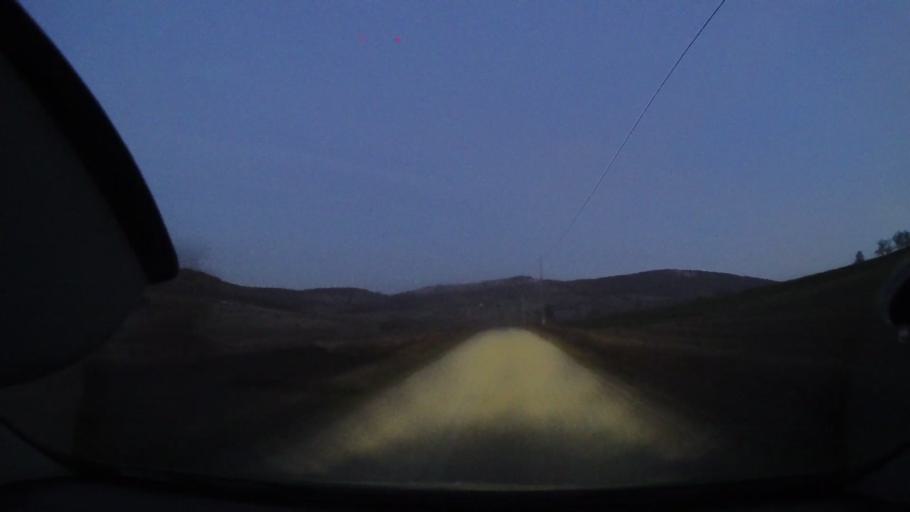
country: RO
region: Bihor
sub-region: Comuna Varciorog
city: Varciorog
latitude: 46.9890
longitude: 22.3258
